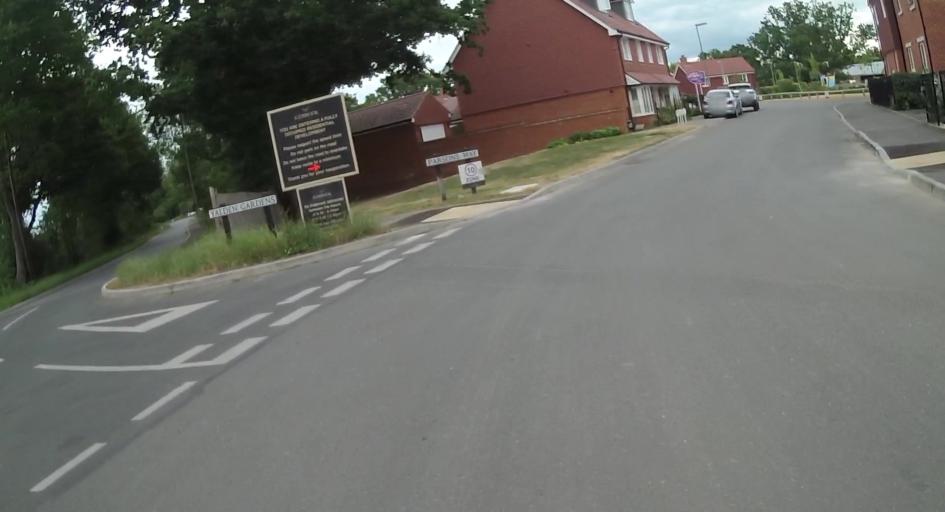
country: GB
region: England
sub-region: Surrey
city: Seale
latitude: 51.2389
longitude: -0.7282
